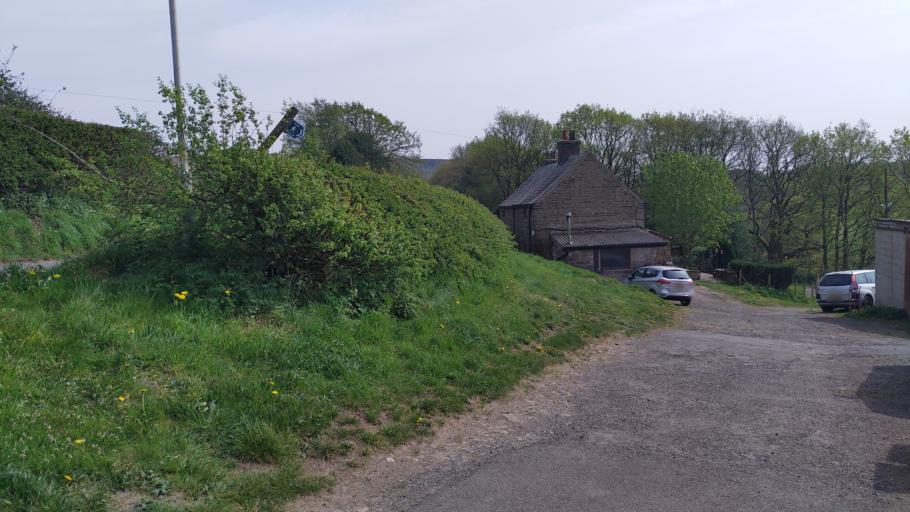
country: GB
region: England
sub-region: Lancashire
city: Chorley
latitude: 53.6698
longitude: -2.5906
